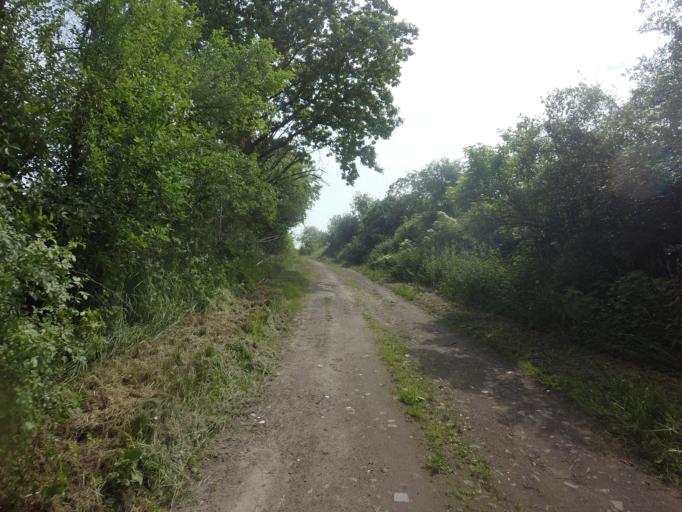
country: PL
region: West Pomeranian Voivodeship
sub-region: Powiat choszczenski
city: Recz
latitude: 53.2872
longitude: 15.4785
